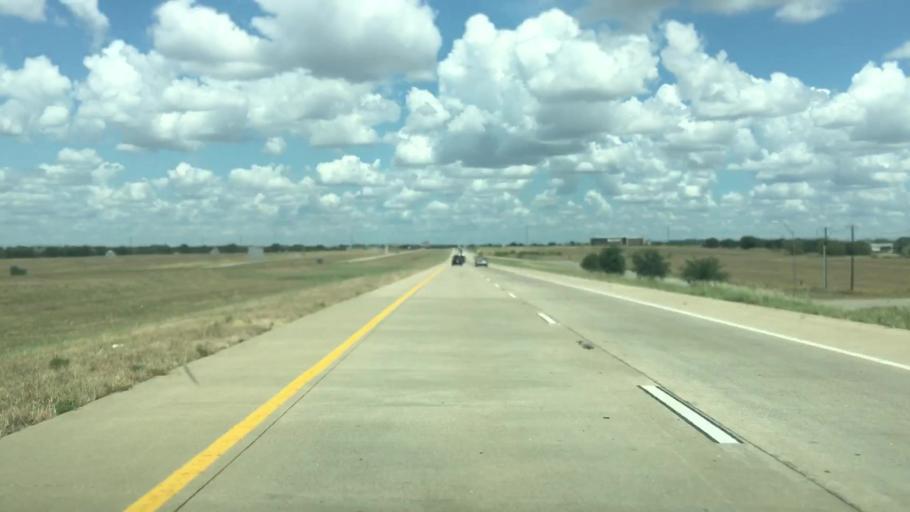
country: US
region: Texas
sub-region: Williamson County
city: Hutto
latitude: 30.5396
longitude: -97.5762
